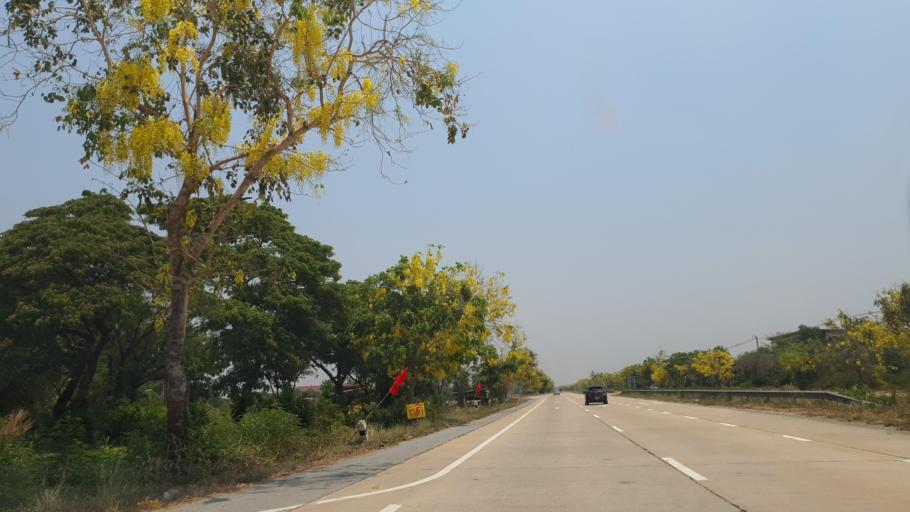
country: TH
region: Suphan Buri
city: Suphan Buri
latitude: 14.5231
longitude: 100.0559
